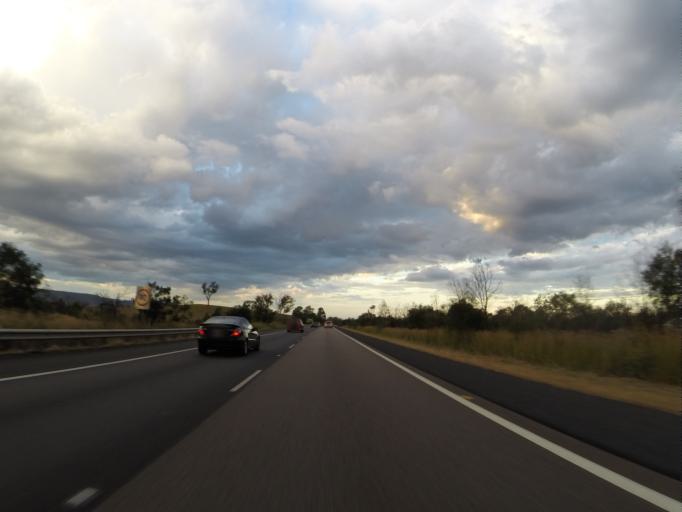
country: AU
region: New South Wales
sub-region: Wollondilly
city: Douglas Park
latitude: -34.2217
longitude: 150.6751
